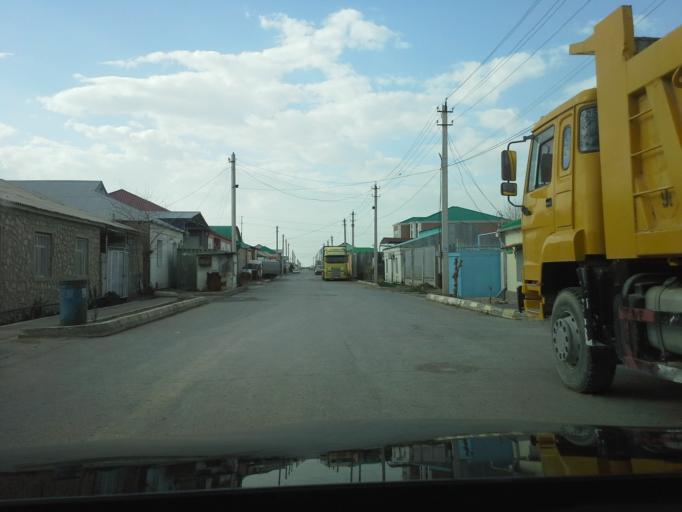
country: TM
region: Ahal
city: Ashgabat
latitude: 37.9901
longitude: 58.2948
